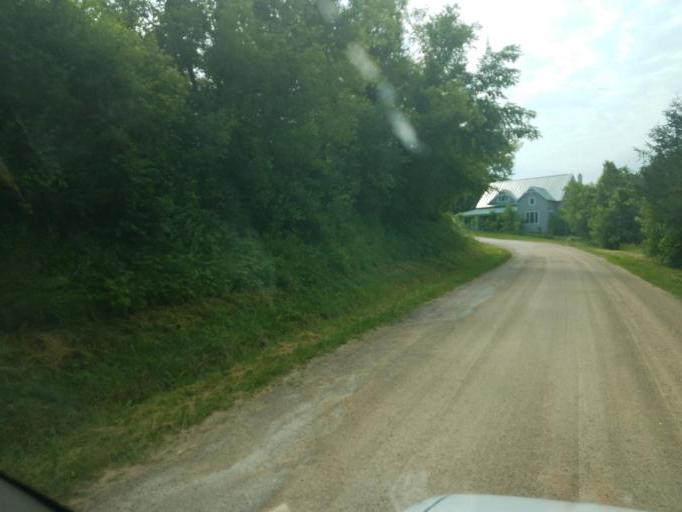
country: US
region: Wisconsin
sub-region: Monroe County
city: Cashton
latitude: 43.7228
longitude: -90.6516
